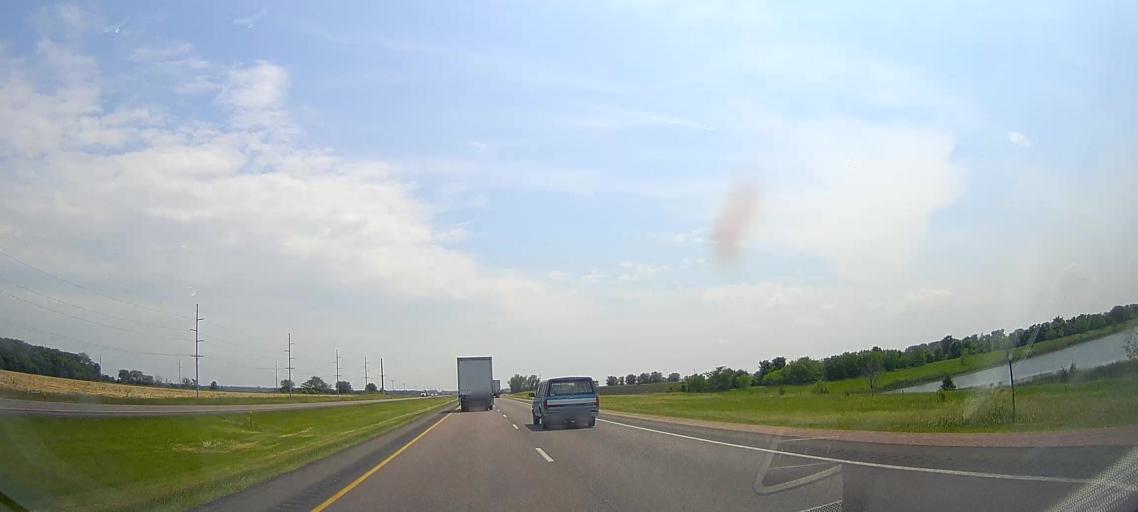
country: US
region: South Dakota
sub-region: Union County
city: Beresford
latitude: 43.1159
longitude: -96.7966
